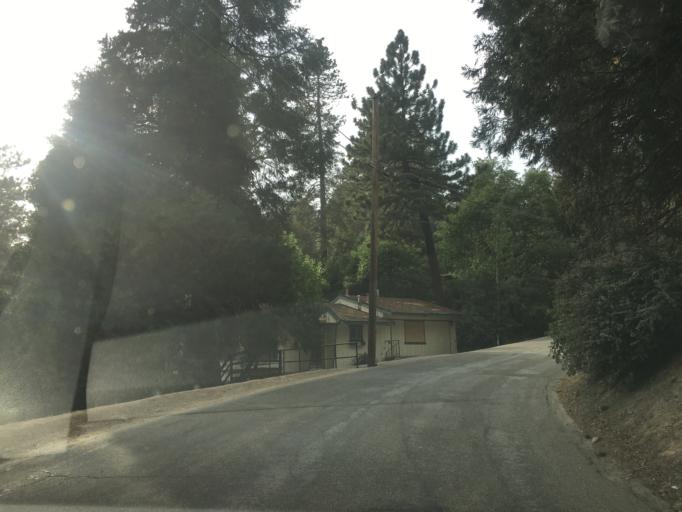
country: US
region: California
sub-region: San Bernardino County
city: Crestline
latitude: 34.2442
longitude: -117.2767
